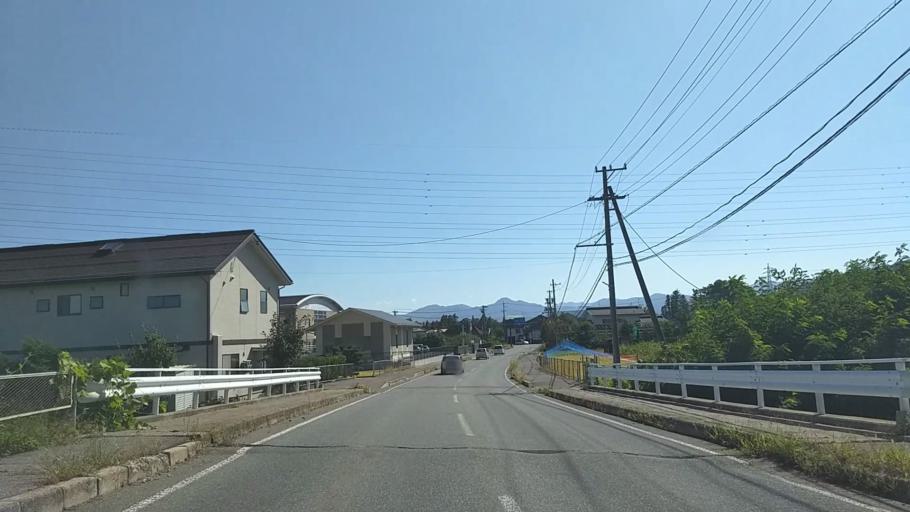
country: JP
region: Nagano
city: Nagano-shi
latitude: 36.6184
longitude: 138.1417
